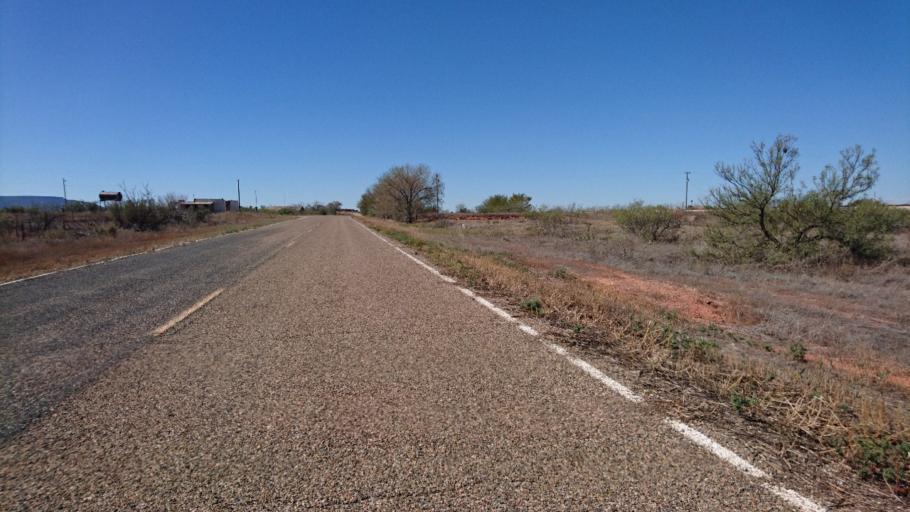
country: US
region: New Mexico
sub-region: Quay County
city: Tucumcari
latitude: 35.0974
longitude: -104.0600
